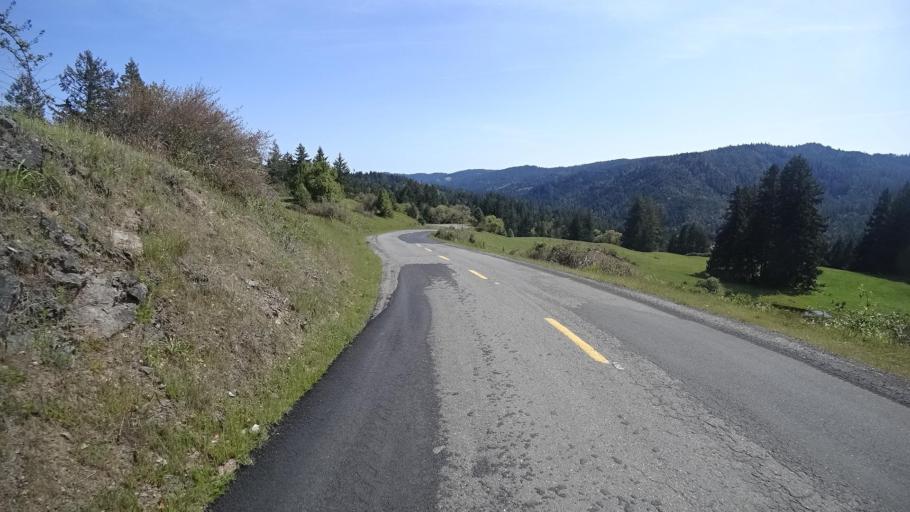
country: US
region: California
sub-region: Humboldt County
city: Redway
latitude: 40.3912
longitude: -123.7465
